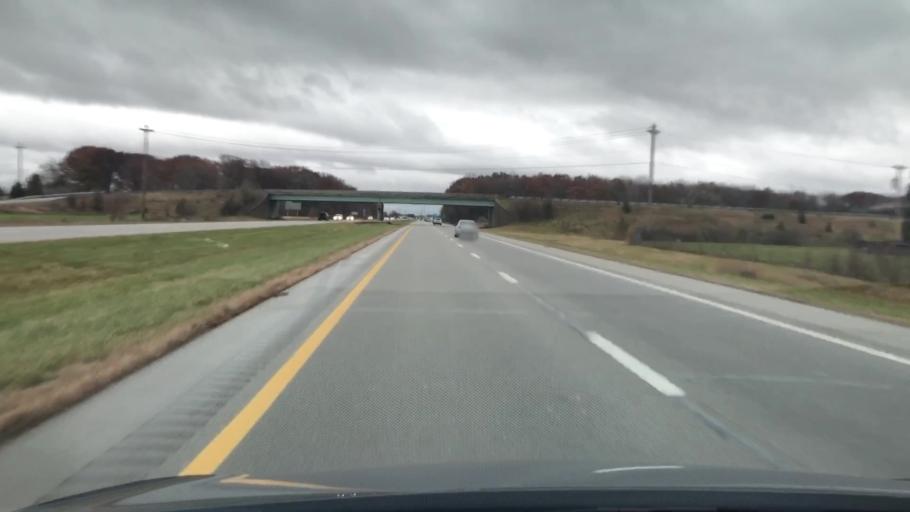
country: US
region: Ohio
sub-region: Wood County
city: Walbridge
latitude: 41.5745
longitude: -83.4696
